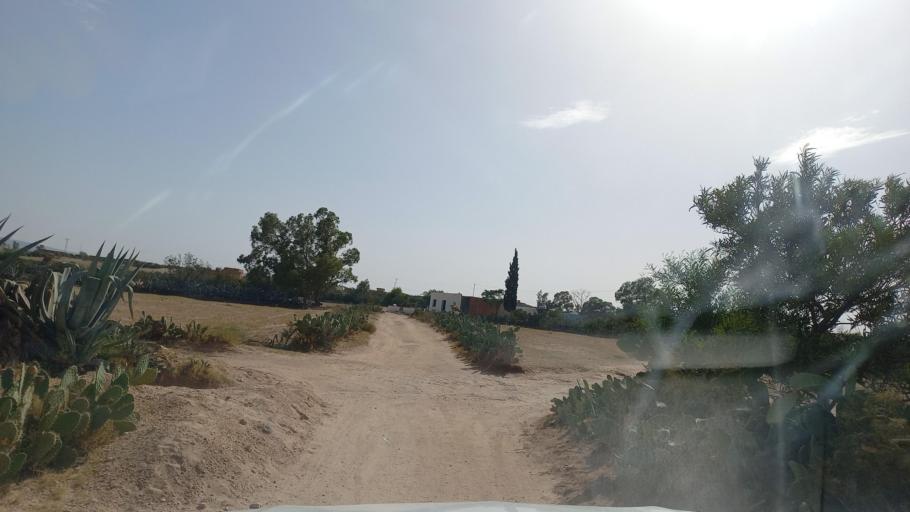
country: TN
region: Al Qasrayn
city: Kasserine
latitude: 35.2791
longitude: 8.9452
